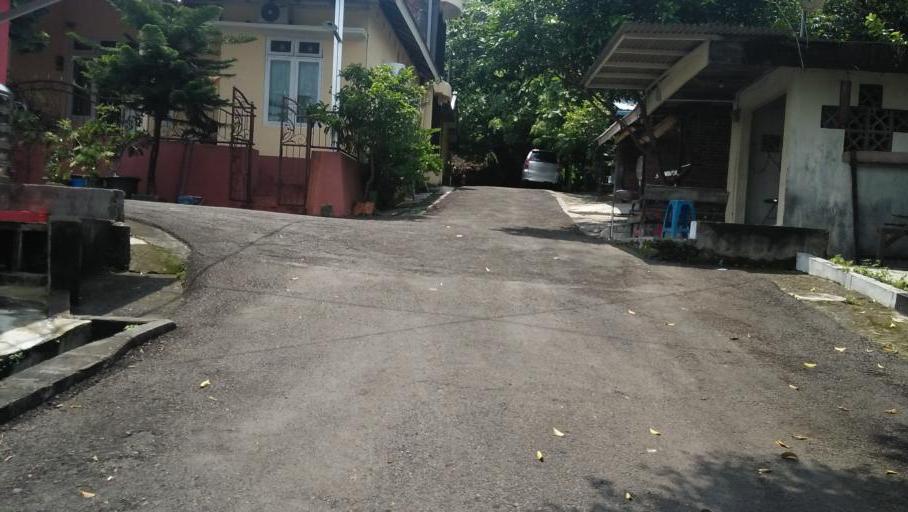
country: ID
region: Central Java
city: Semarang
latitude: -7.0335
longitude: 110.4516
